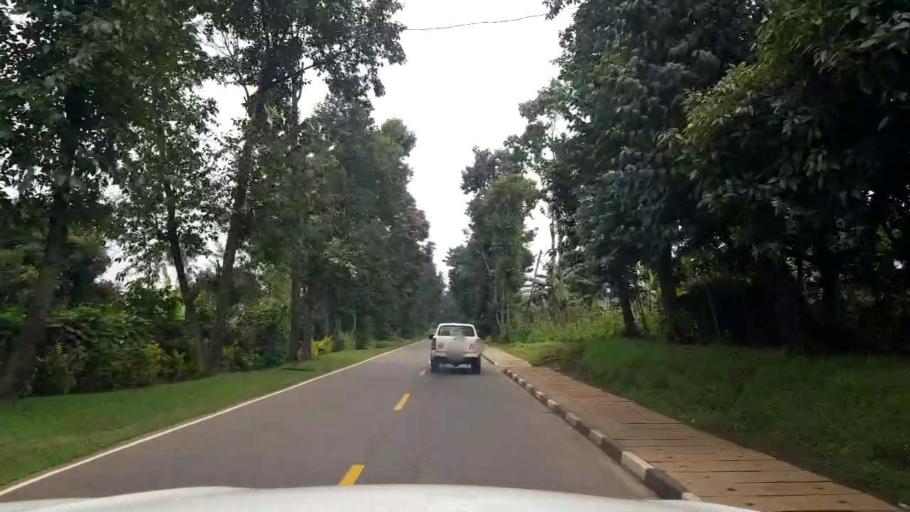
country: RW
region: Northern Province
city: Musanze
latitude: -1.4579
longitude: 29.6113
